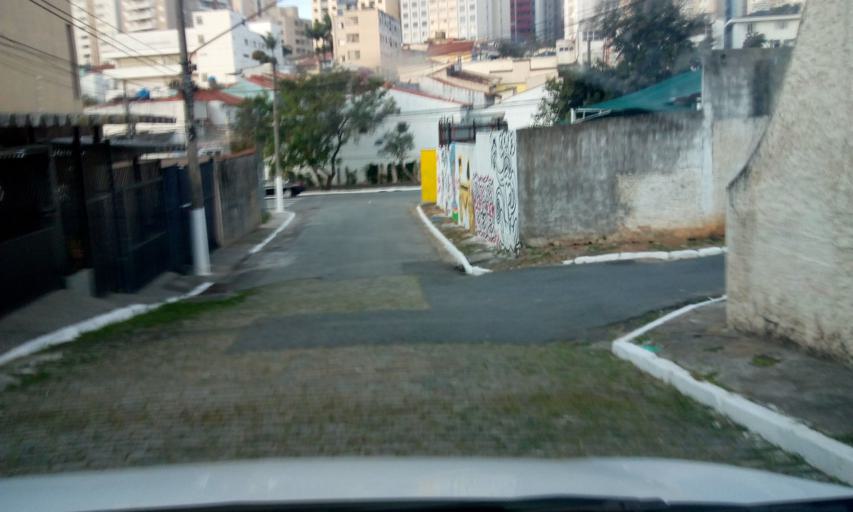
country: BR
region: Sao Paulo
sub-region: Diadema
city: Diadema
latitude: -23.6206
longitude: -46.6431
